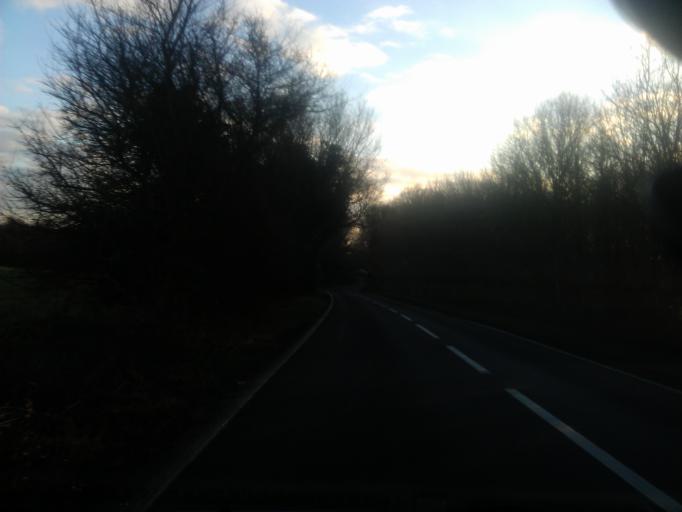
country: GB
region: England
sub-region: Essex
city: Witham
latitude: 51.8401
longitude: 0.6447
